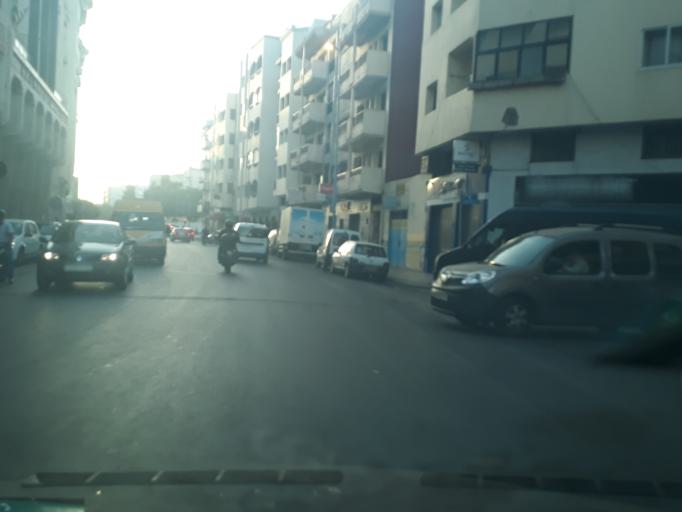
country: MA
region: Grand Casablanca
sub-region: Casablanca
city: Casablanca
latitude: 33.5743
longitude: -7.6421
